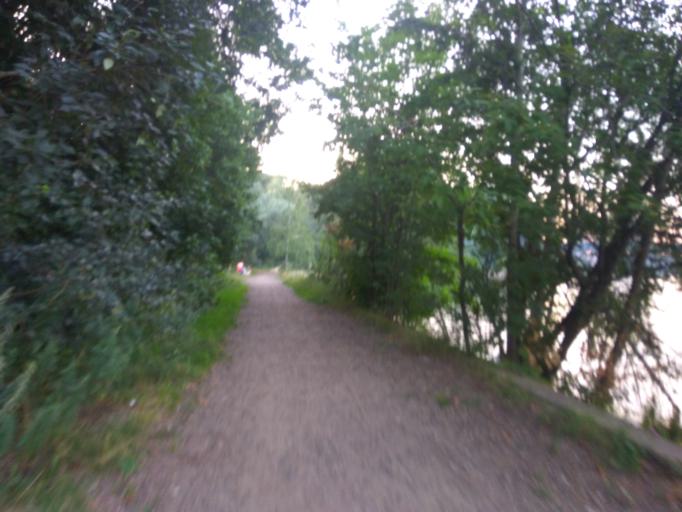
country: RU
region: Moskovskaya
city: Levoberezhnaya
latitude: 55.8791
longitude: 37.4569
